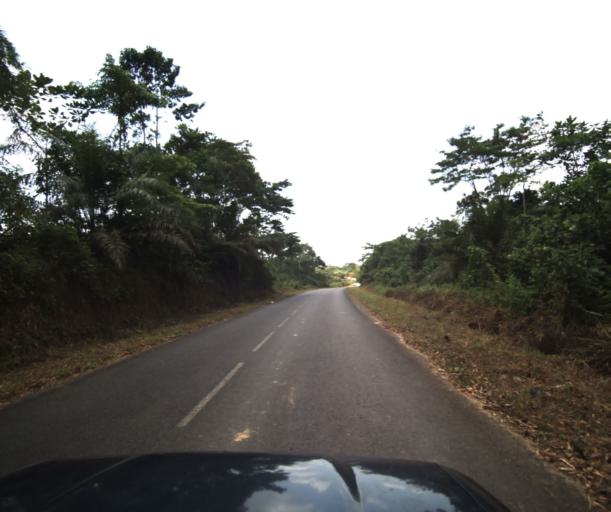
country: CM
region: Centre
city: Eseka
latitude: 3.7052
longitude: 10.7906
